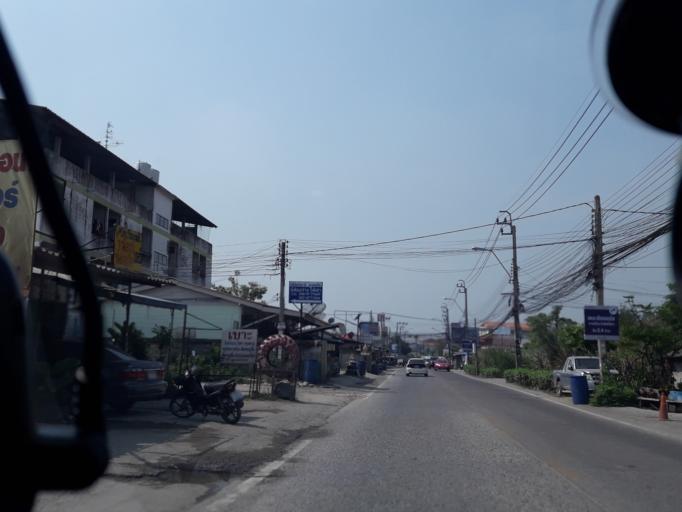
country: TH
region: Bangkok
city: Khlong Sam Wa
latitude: 13.8418
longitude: 100.7147
